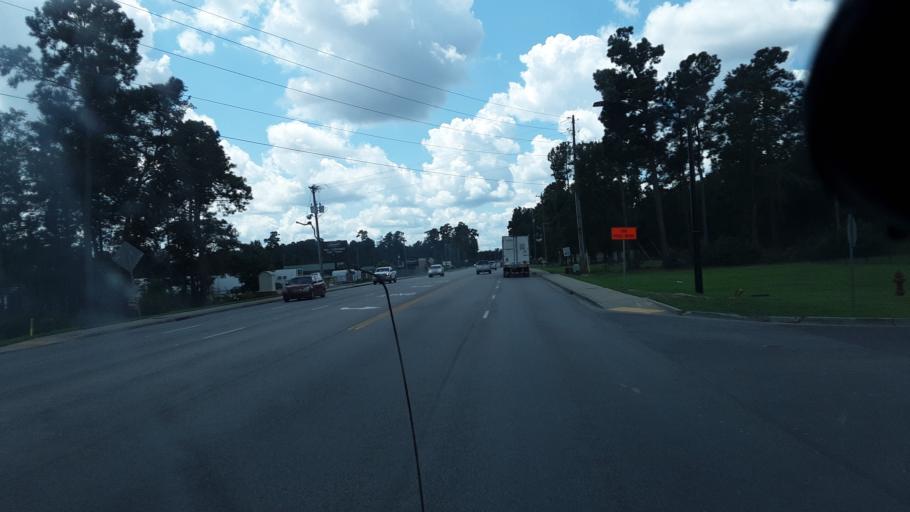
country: US
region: South Carolina
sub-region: Berkeley County
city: Sangaree
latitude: 33.0546
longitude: -80.1008
